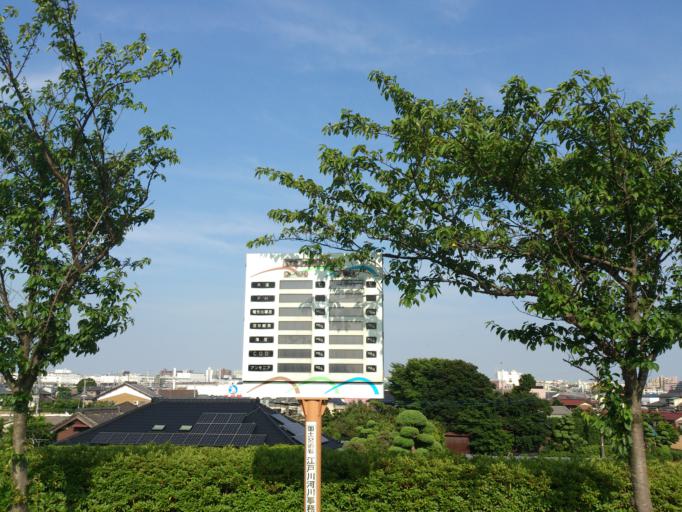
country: JP
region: Chiba
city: Matsudo
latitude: 35.7986
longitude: 139.8938
